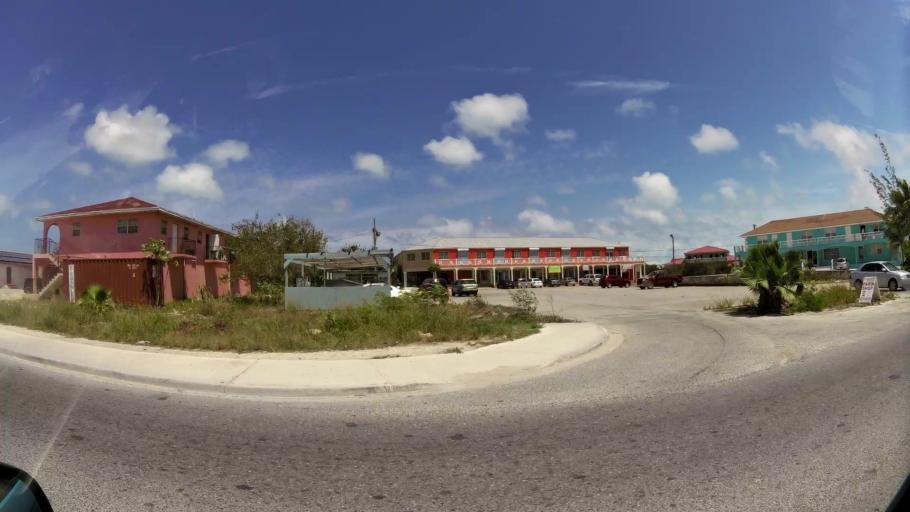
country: BS
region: Mayaguana
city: Abraham's Bay
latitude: 21.7757
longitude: -72.2548
